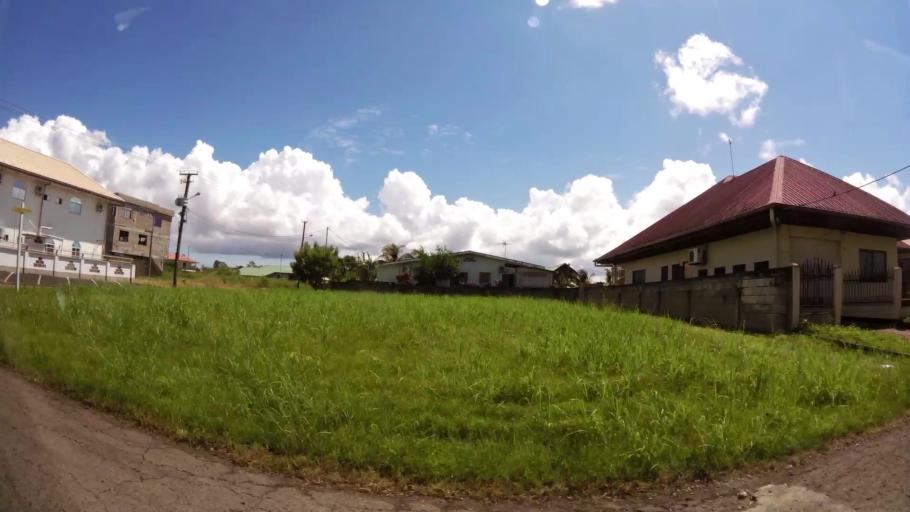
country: SR
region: Paramaribo
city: Paramaribo
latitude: 5.8611
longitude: -55.1320
